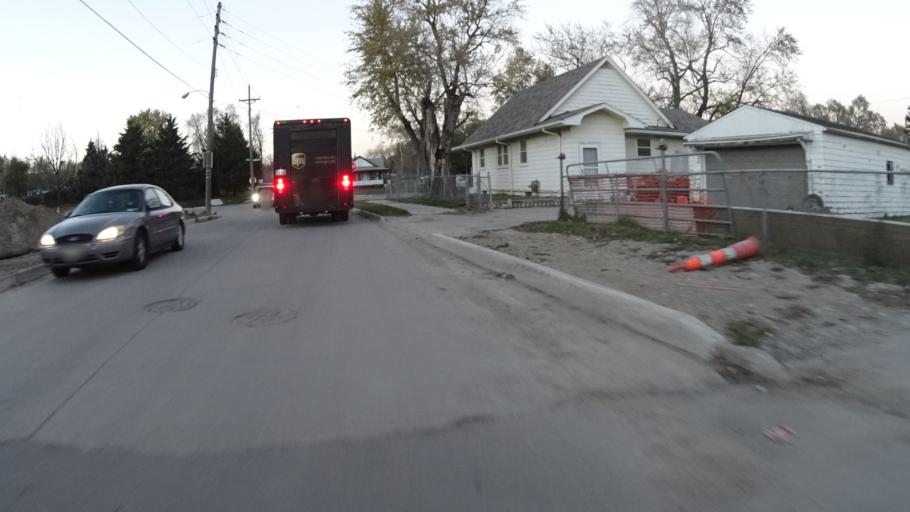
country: US
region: Nebraska
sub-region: Douglas County
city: Omaha
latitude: 41.1941
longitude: -95.9456
